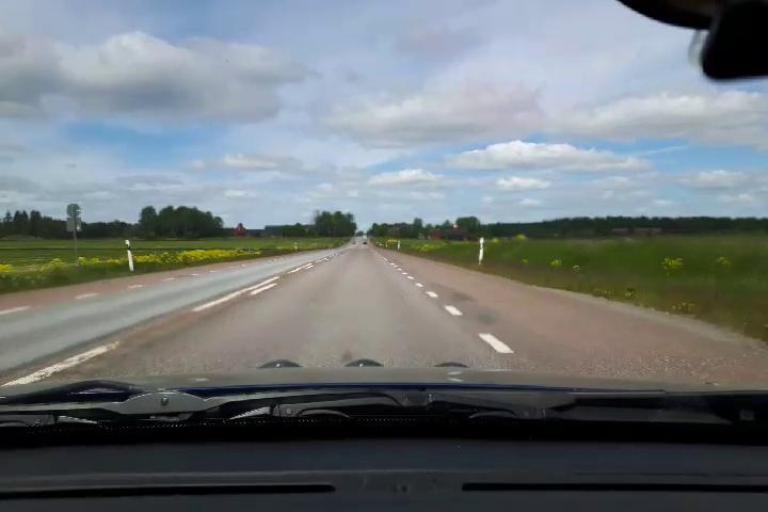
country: SE
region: Uppsala
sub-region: Uppsala Kommun
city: Gamla Uppsala
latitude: 59.9402
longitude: 17.5931
